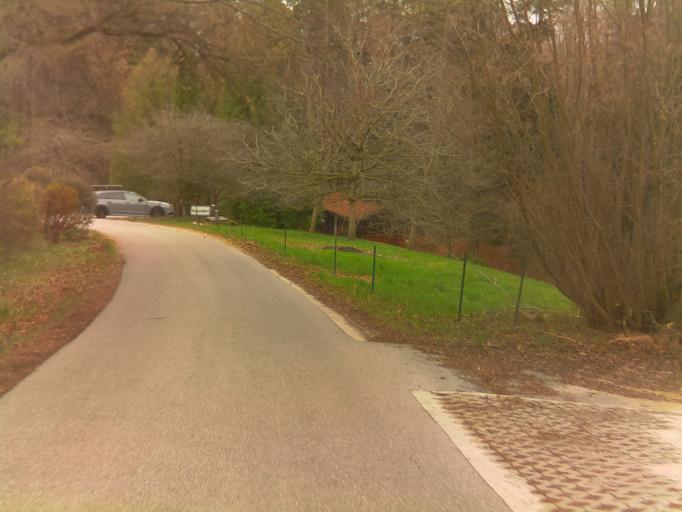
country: DE
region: Bavaria
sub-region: Upper Bavaria
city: Peissenberg
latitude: 47.8034
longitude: 11.0438
